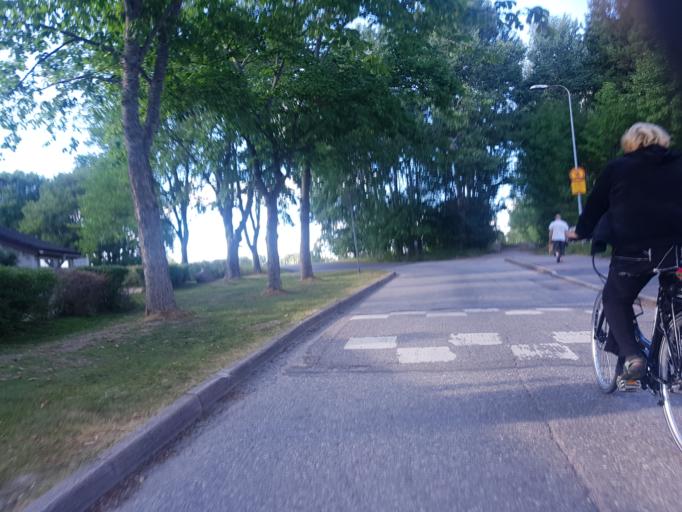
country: FI
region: Uusimaa
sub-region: Helsinki
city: Vantaa
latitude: 60.2718
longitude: 24.9837
